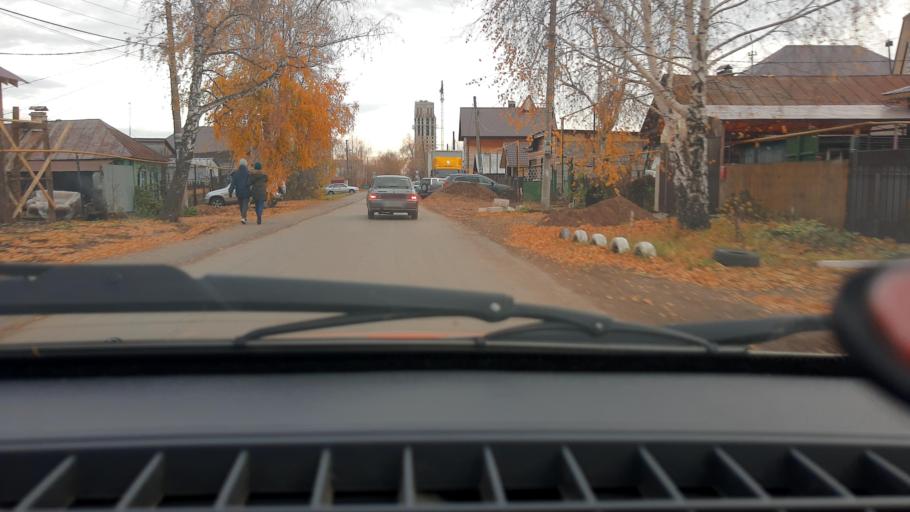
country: RU
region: Bashkortostan
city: Avdon
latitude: 54.7009
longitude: 55.8190
